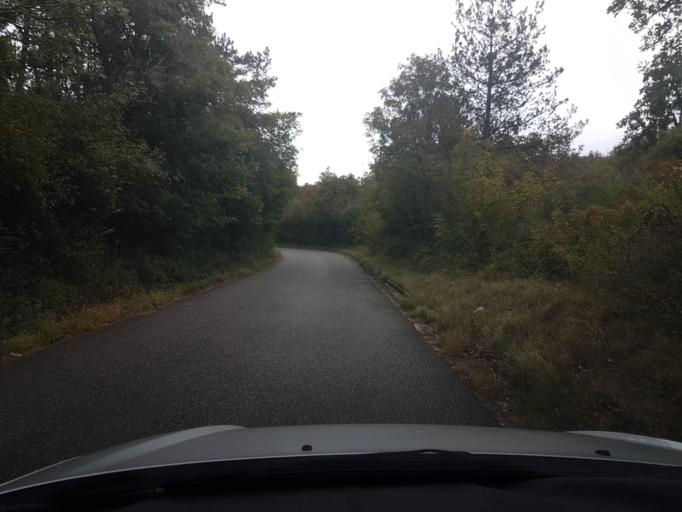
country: IT
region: Friuli Venezia Giulia
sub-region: Provincia di Gorizia
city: Doberdo del Lago
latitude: 45.8321
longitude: 13.5501
